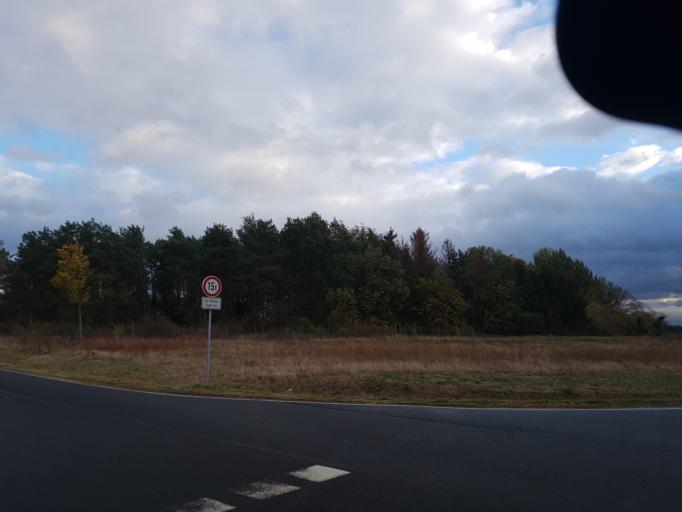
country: DE
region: Saxony-Anhalt
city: Seyda
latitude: 51.8853
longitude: 12.8947
